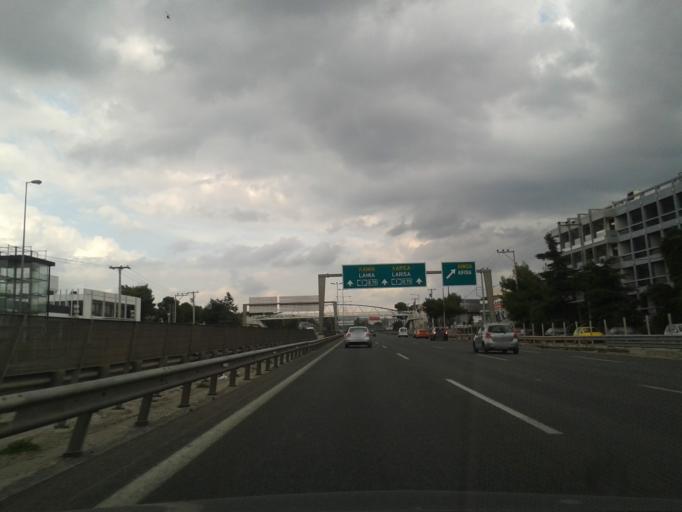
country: GR
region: Attica
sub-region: Nomarchia Athinas
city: Lykovrysi
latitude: 38.0903
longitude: 23.7903
